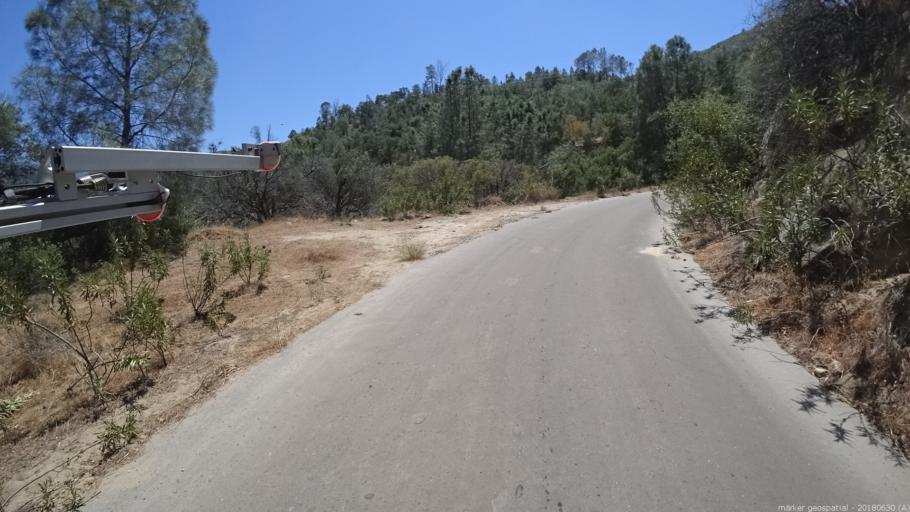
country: US
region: California
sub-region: Fresno County
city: Auberry
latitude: 37.1530
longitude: -119.4043
